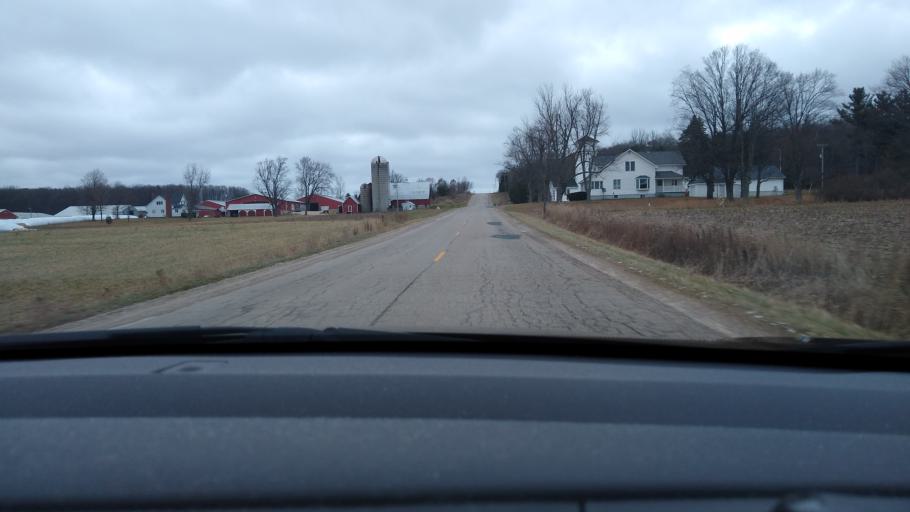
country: US
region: Michigan
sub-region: Missaukee County
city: Lake City
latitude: 44.2856
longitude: -85.0542
